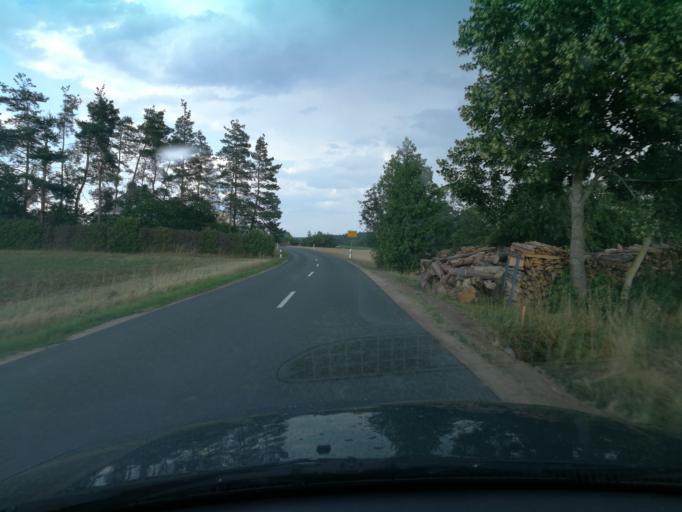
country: DE
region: Bavaria
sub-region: Regierungsbezirk Mittelfranken
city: Langenzenn
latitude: 49.4652
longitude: 10.7941
